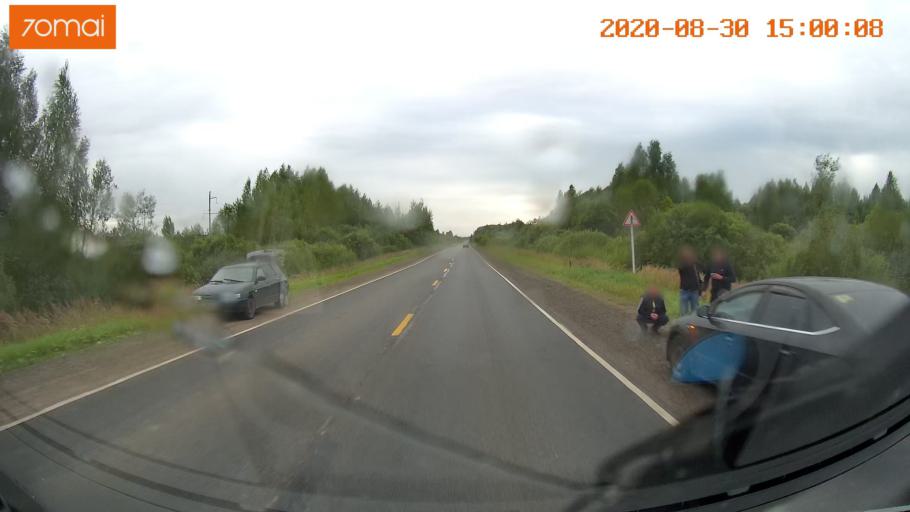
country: RU
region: Ivanovo
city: Staraya Vichuga
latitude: 57.3344
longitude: 41.9622
